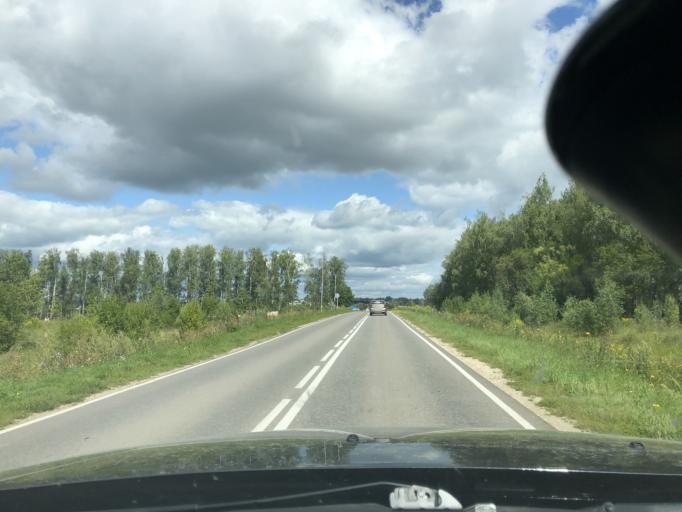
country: RU
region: Tula
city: Yasnogorsk
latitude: 54.4602
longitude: 37.7089
